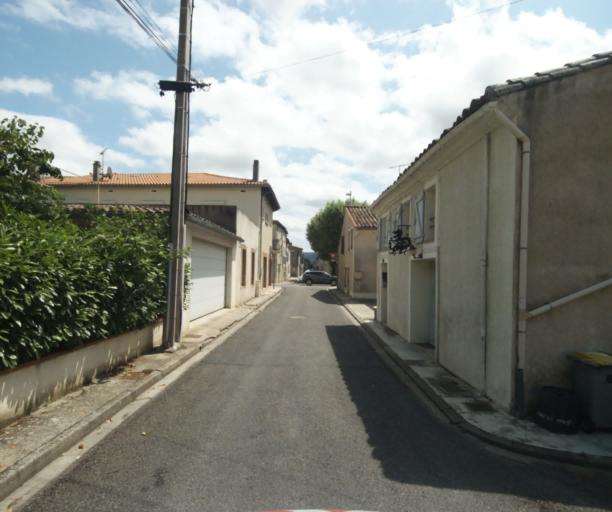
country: FR
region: Midi-Pyrenees
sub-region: Departement de la Haute-Garonne
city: Revel
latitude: 43.4588
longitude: 2.0011
